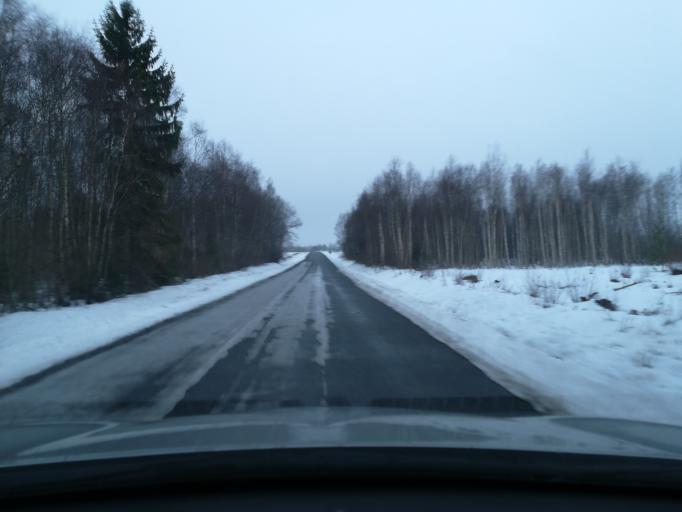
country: EE
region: Harju
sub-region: Raasiku vald
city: Raasiku
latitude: 59.3401
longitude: 25.2425
